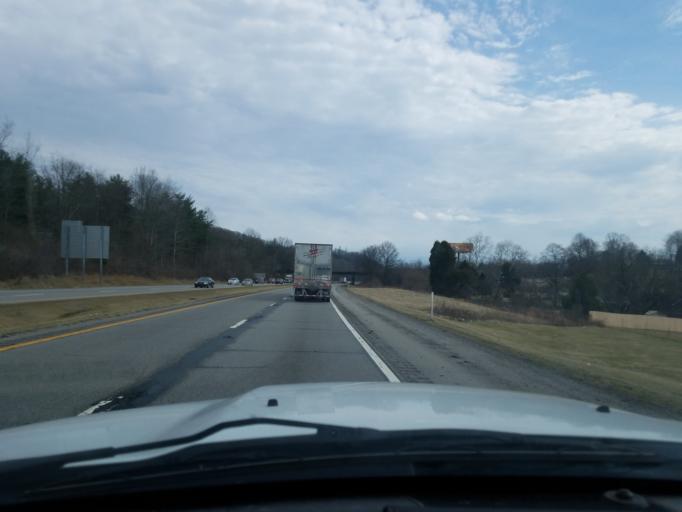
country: US
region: West Virginia
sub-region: Kanawha County
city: Nitro
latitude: 38.4538
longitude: -81.8640
